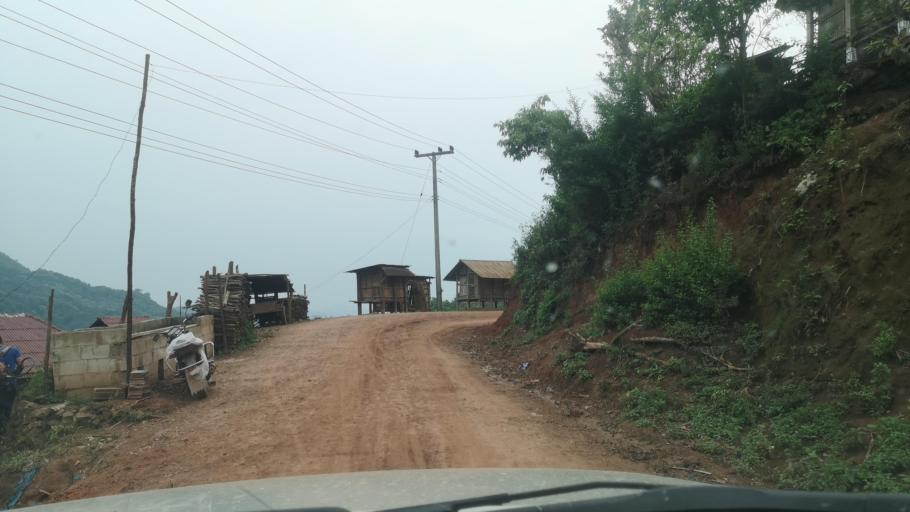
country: LA
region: Oudomxai
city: Muang La
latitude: 21.1311
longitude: 101.8795
